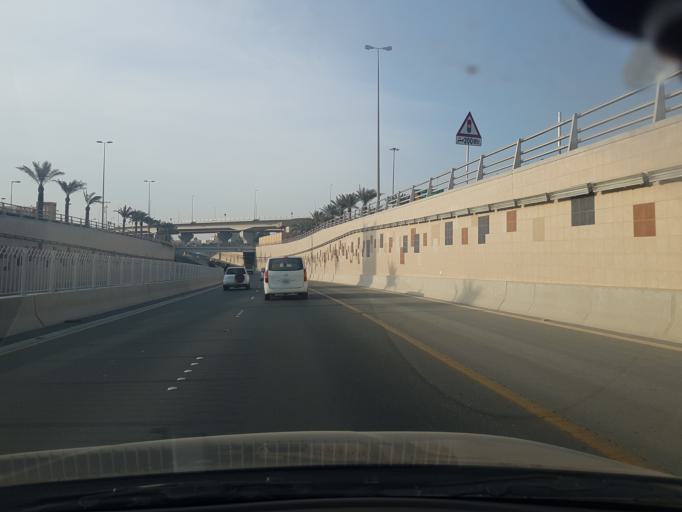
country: BH
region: Northern
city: Madinat `Isa
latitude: 26.1669
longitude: 50.5431
